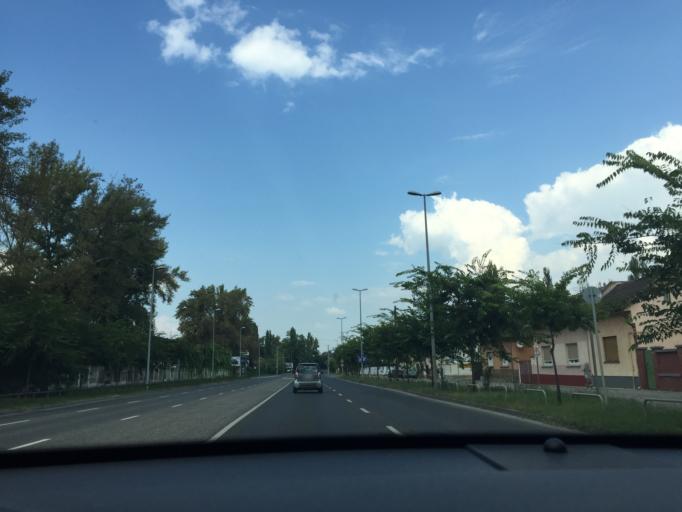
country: HU
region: Budapest
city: Budapest IV. keruelet
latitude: 47.5858
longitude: 19.0823
